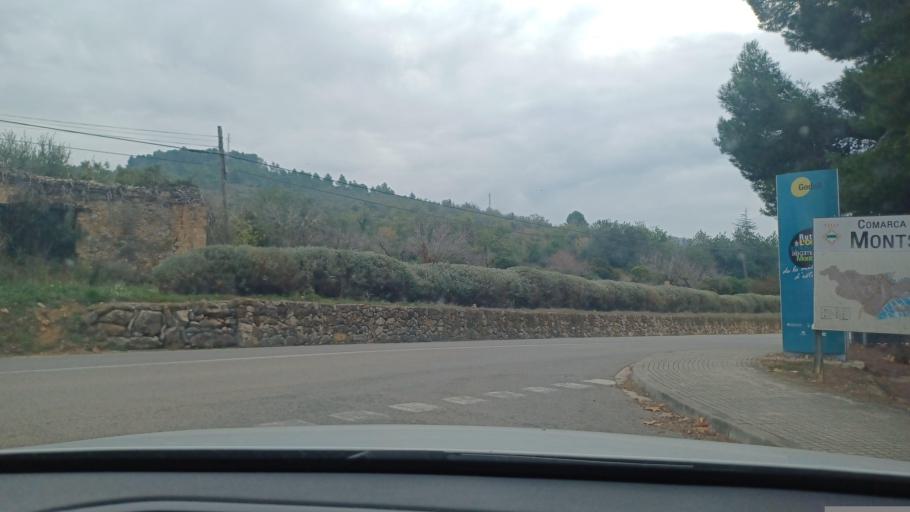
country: ES
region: Catalonia
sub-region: Provincia de Tarragona
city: Santa Barbara
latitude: 40.6603
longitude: 0.4653
